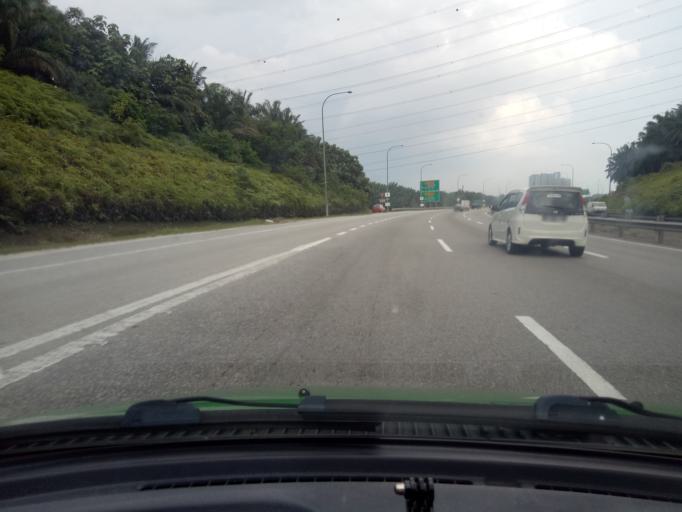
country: MY
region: Selangor
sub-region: Hulu Langat
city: Semenyih
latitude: 2.9785
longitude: 101.8360
